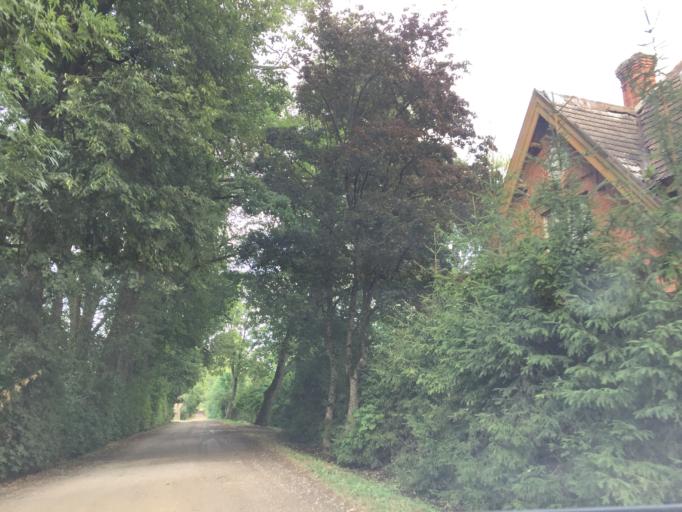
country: LT
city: Zagare
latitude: 56.3626
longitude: 23.2654
